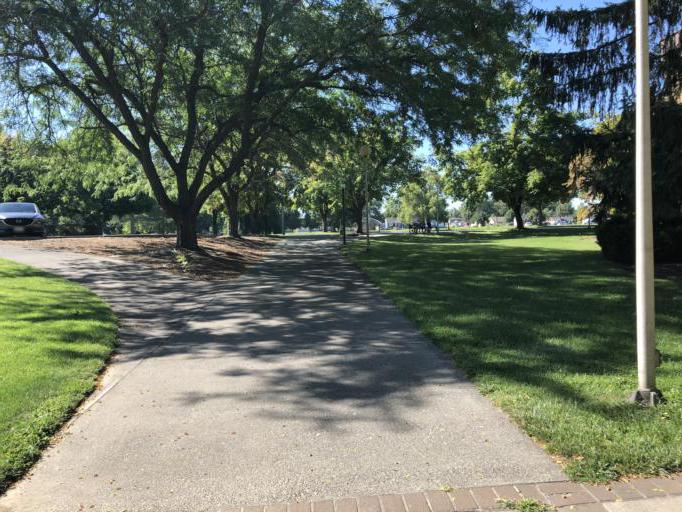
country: US
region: Washington
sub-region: Walla Walla County
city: College Place
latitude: 46.0462
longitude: -118.3927
